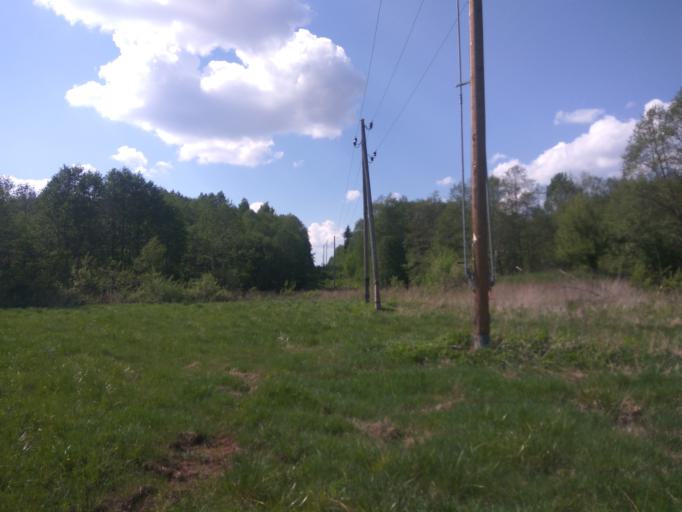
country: LV
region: Kuldigas Rajons
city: Kuldiga
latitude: 57.1741
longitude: 22.0223
